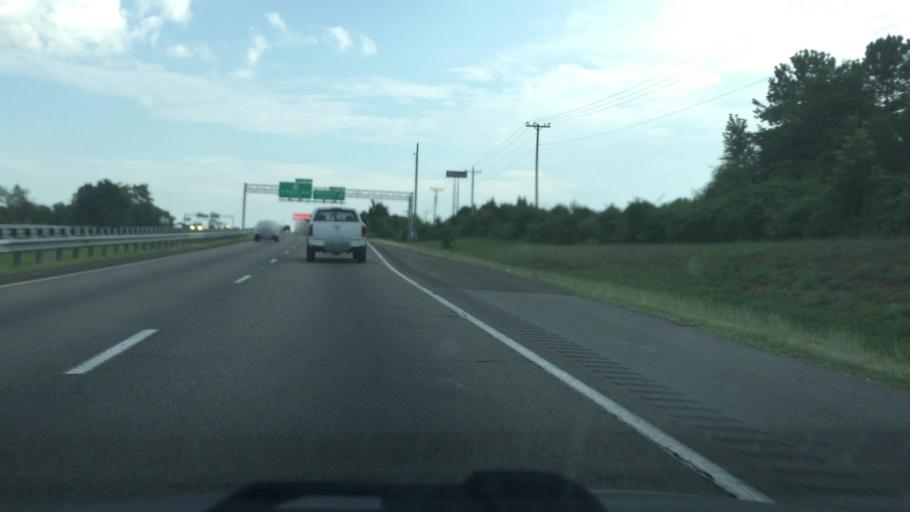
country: US
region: North Carolina
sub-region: Iredell County
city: Statesville
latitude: 35.7794
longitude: -80.8638
